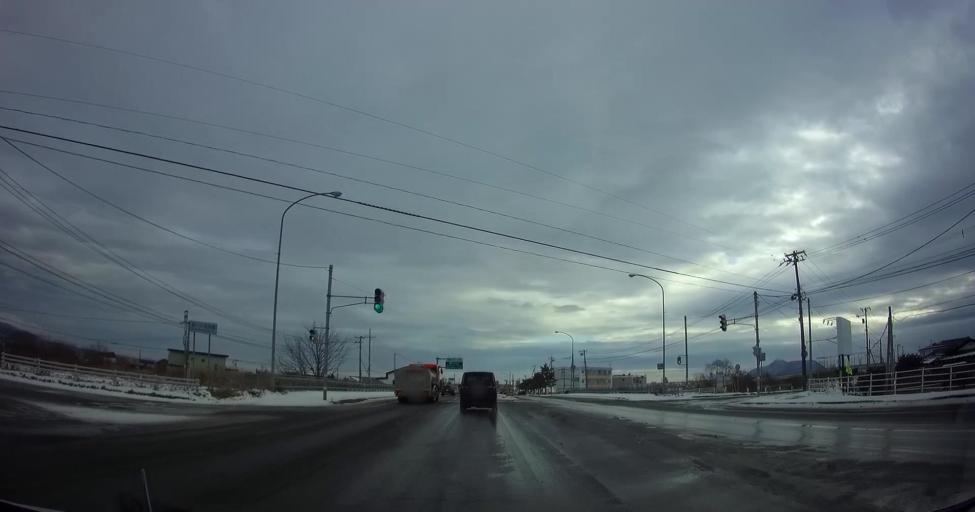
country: JP
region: Hokkaido
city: Nanae
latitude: 41.8388
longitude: 140.6900
